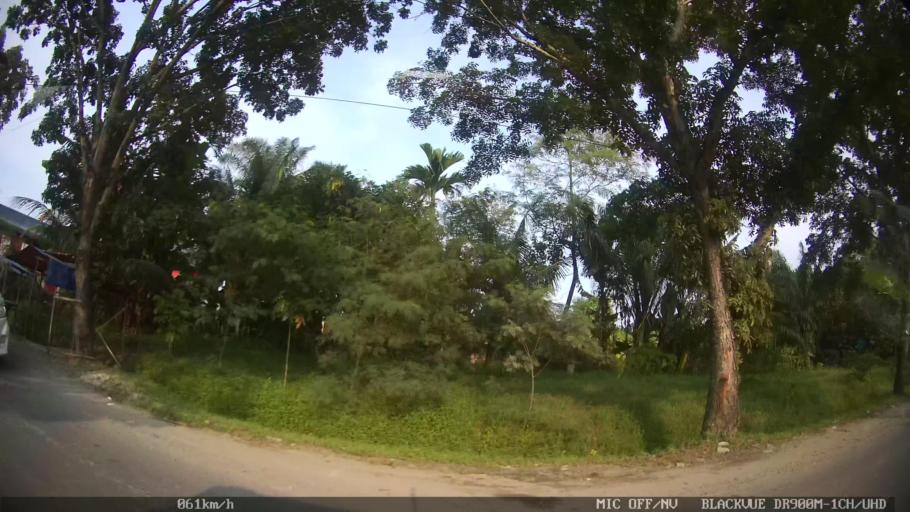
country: ID
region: North Sumatra
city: Binjai
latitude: 3.6117
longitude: 98.5344
